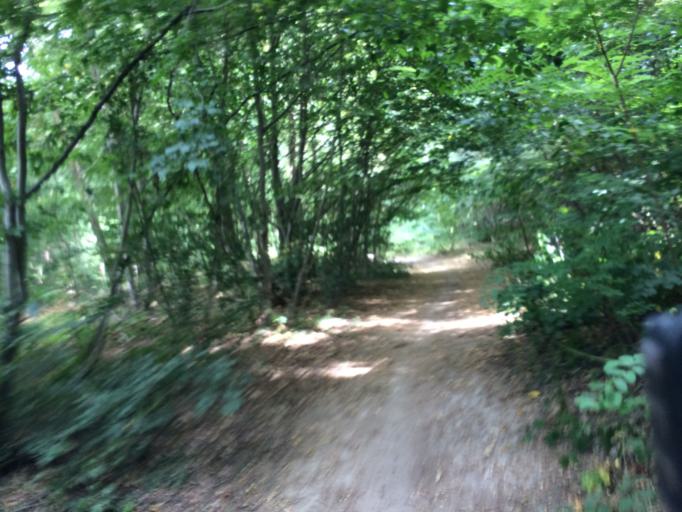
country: FR
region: Ile-de-France
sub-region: Departement de l'Essonne
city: Draveil
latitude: 48.6795
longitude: 2.4364
